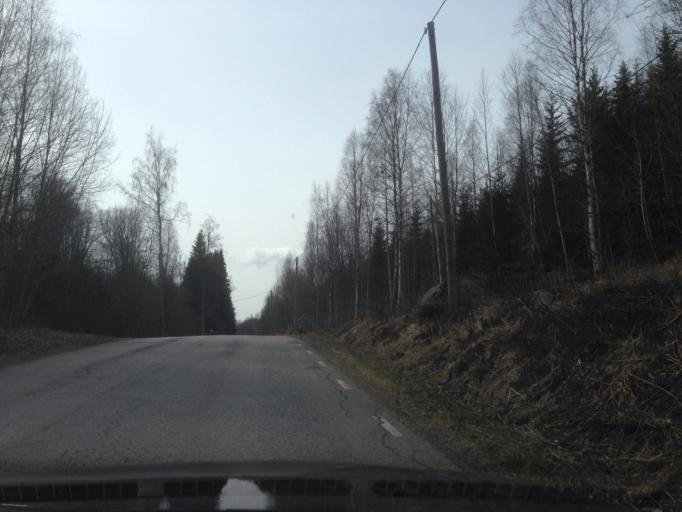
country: SE
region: Dalarna
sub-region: Ludvika Kommun
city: Grangesberg
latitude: 60.0898
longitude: 14.9971
